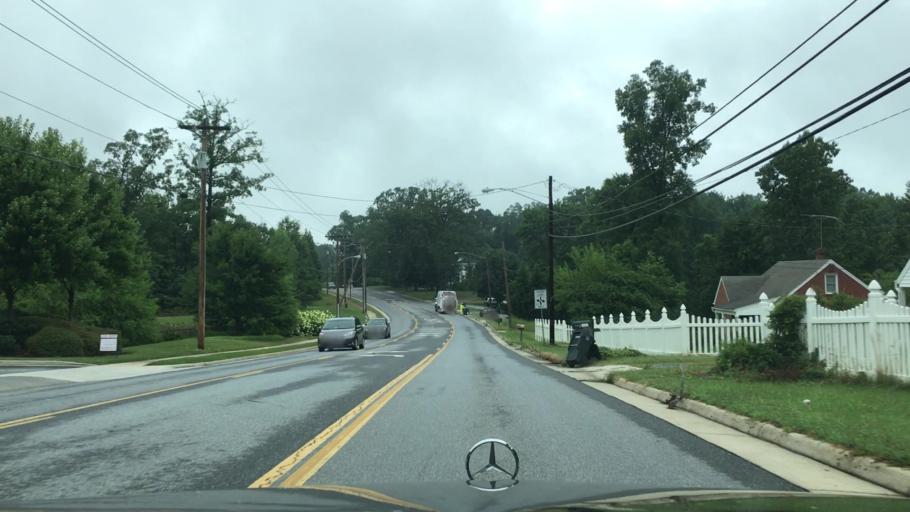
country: US
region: Virginia
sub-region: Campbell County
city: Timberlake
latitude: 37.3556
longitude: -79.2262
